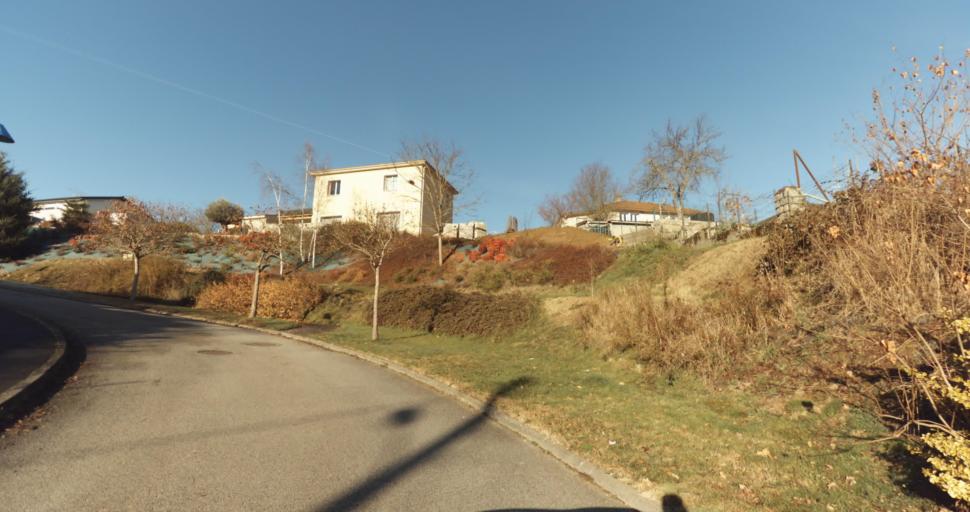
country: FR
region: Limousin
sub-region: Departement de la Haute-Vienne
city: Aixe-sur-Vienne
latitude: 45.7993
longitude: 1.1509
